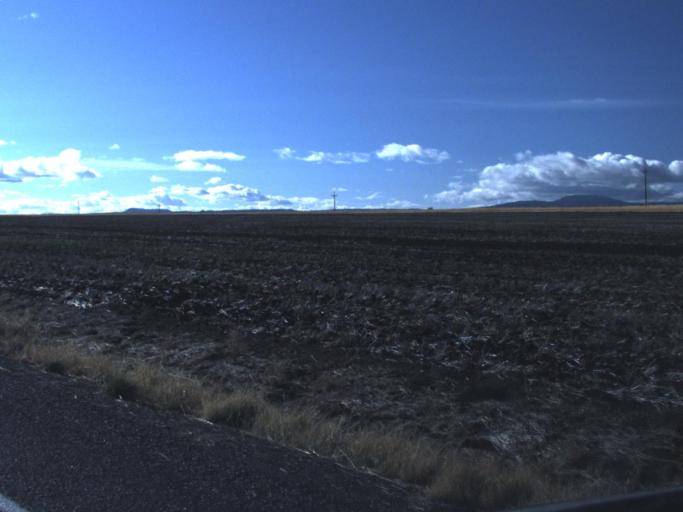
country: US
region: Washington
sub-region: Asotin County
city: Asotin
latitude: 46.2133
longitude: -117.0703
